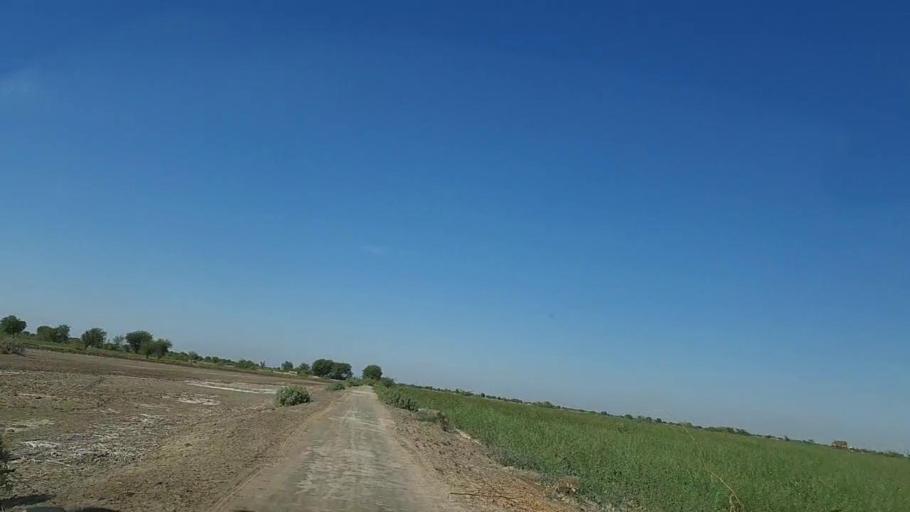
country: PK
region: Sindh
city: Pithoro
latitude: 25.5596
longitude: 69.4598
